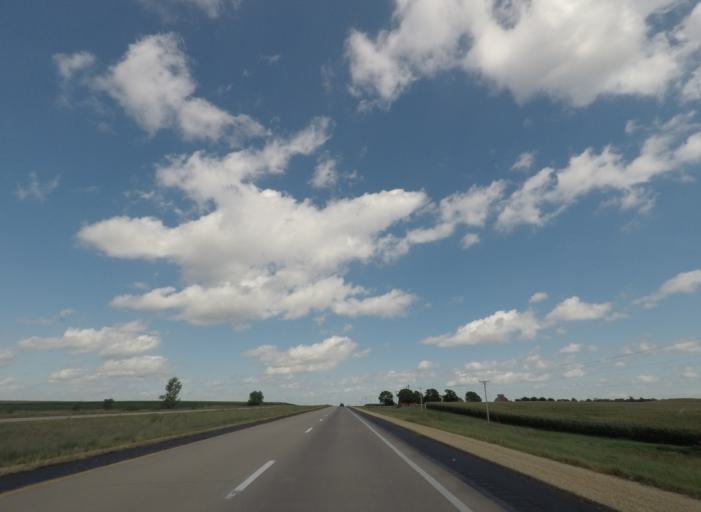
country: US
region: Iowa
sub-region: Jones County
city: Monticello
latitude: 42.2819
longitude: -91.1244
